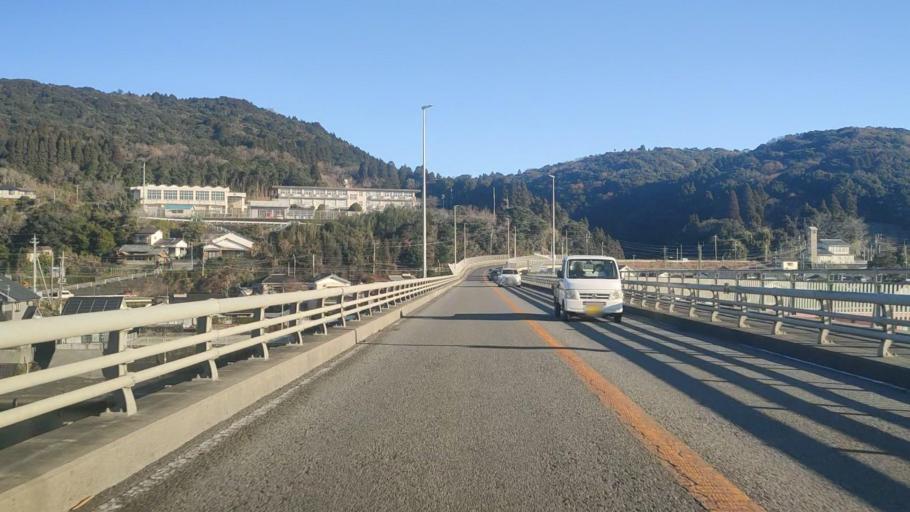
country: JP
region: Miyazaki
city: Takanabe
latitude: 32.3392
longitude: 131.6118
